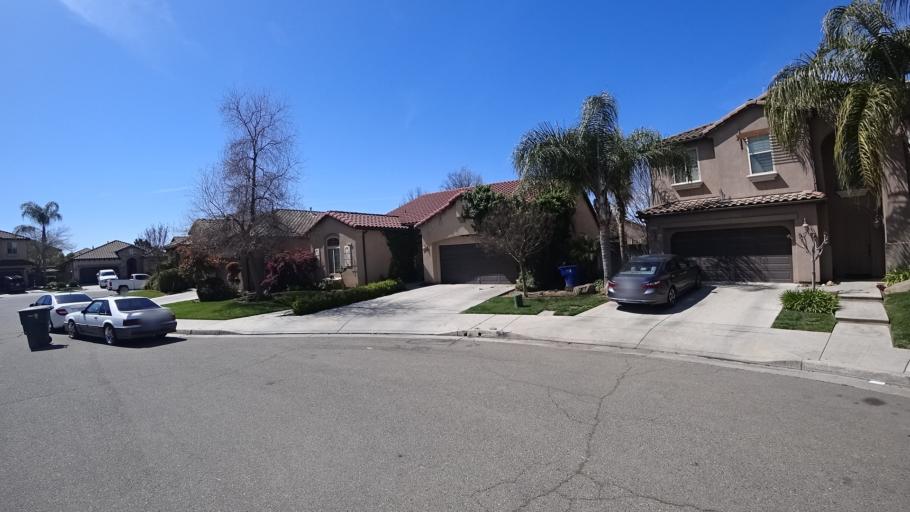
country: US
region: California
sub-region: Fresno County
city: Biola
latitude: 36.8185
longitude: -119.9148
